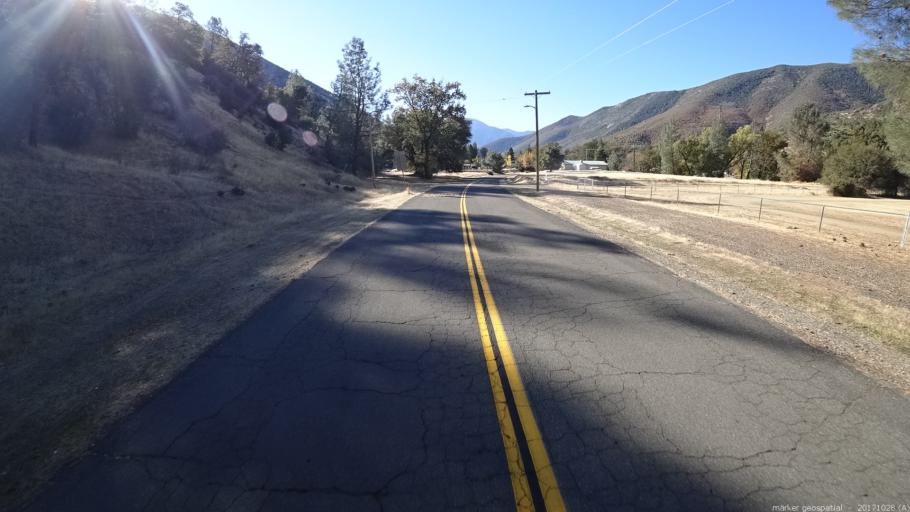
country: US
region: California
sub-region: Trinity County
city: Lewiston
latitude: 40.7074
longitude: -122.6346
